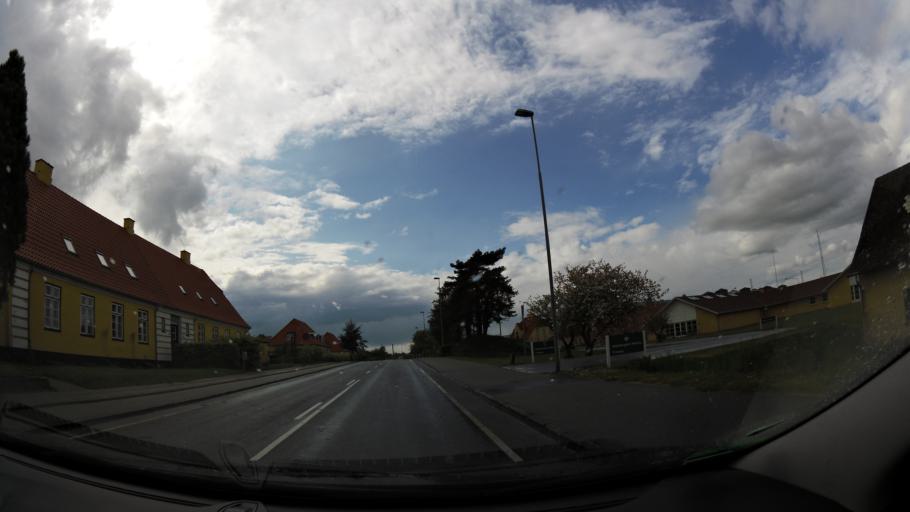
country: DK
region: South Denmark
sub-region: Nyborg Kommune
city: Nyborg
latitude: 55.3102
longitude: 10.7790
